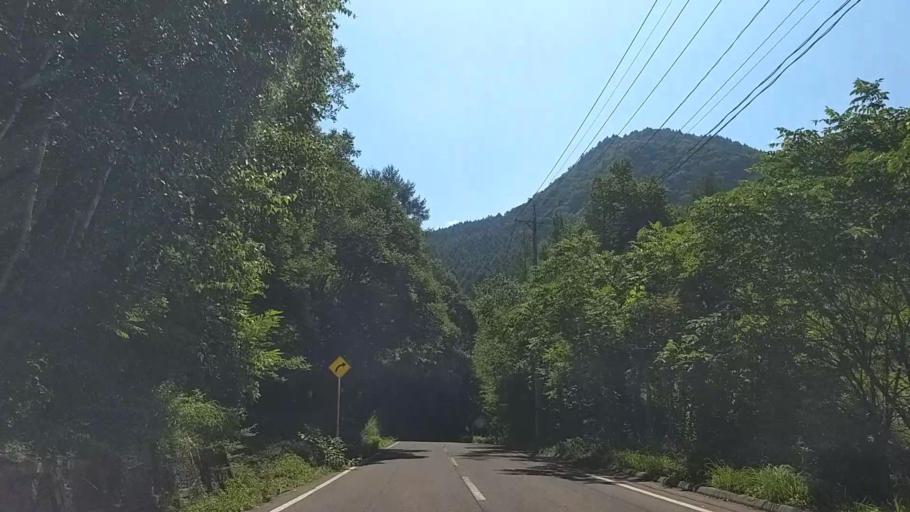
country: JP
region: Nagano
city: Matsumoto
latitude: 36.2067
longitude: 138.0948
